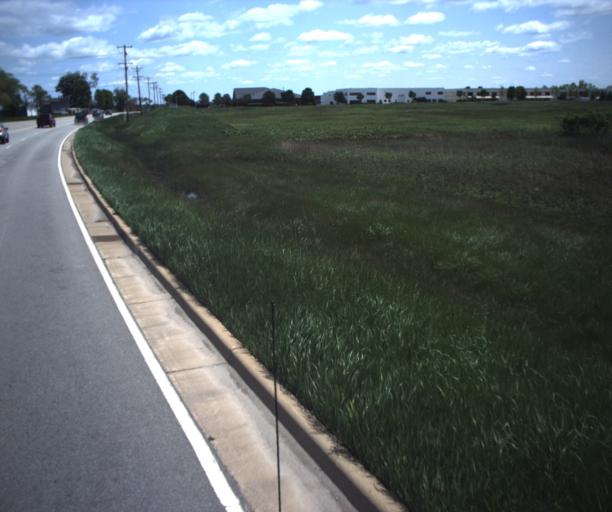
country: US
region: Illinois
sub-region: Kane County
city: Geneva
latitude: 41.8709
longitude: -88.2668
